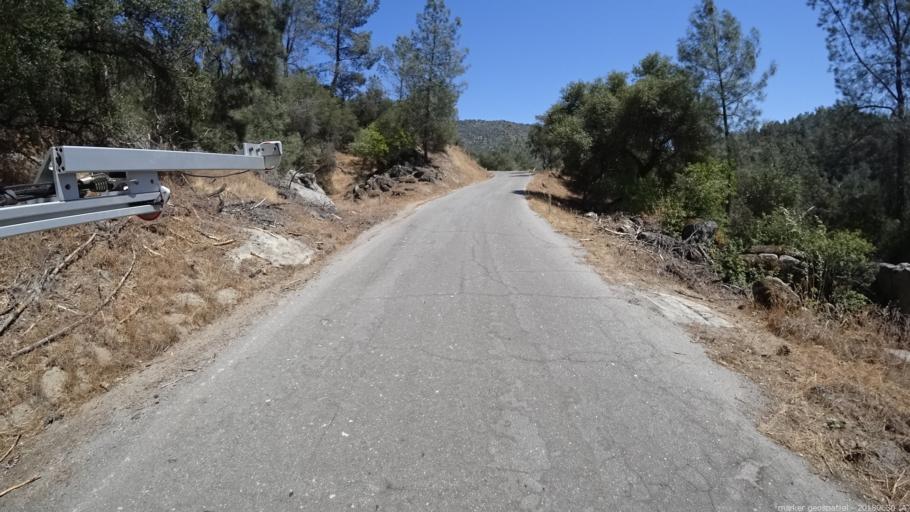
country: US
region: California
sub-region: Fresno County
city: Auberry
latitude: 37.1453
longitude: -119.4954
